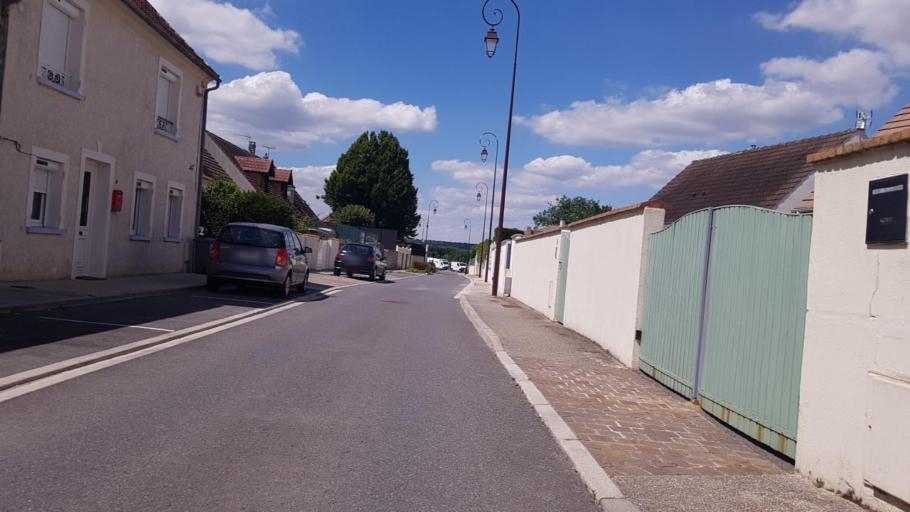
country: FR
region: Ile-de-France
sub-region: Departement de Seine-et-Marne
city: Moussy-le-Vieux
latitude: 49.0357
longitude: 2.6382
